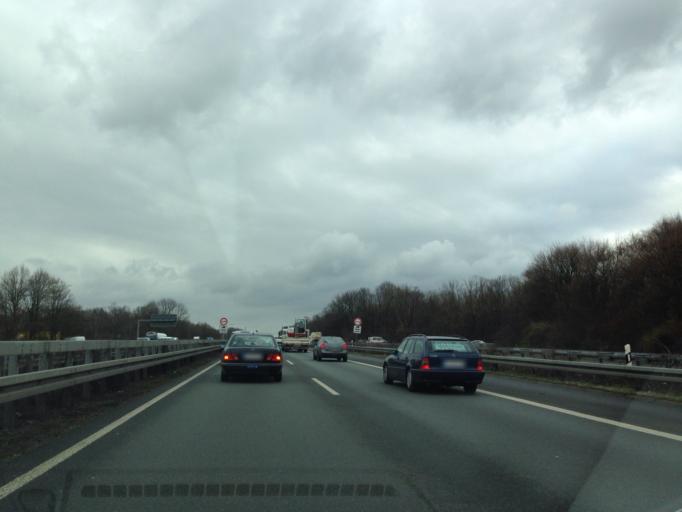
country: DE
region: North Rhine-Westphalia
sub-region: Regierungsbezirk Munster
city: Recklinghausen
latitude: 51.5814
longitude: 7.1900
